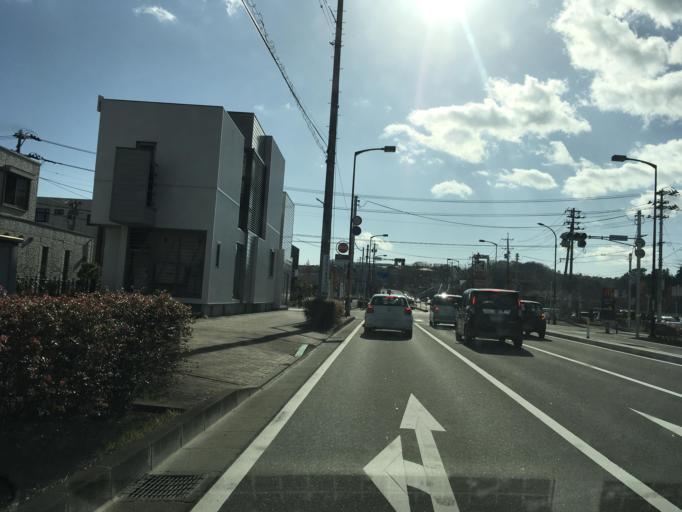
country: JP
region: Miyagi
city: Sendai
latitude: 38.2696
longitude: 140.7616
